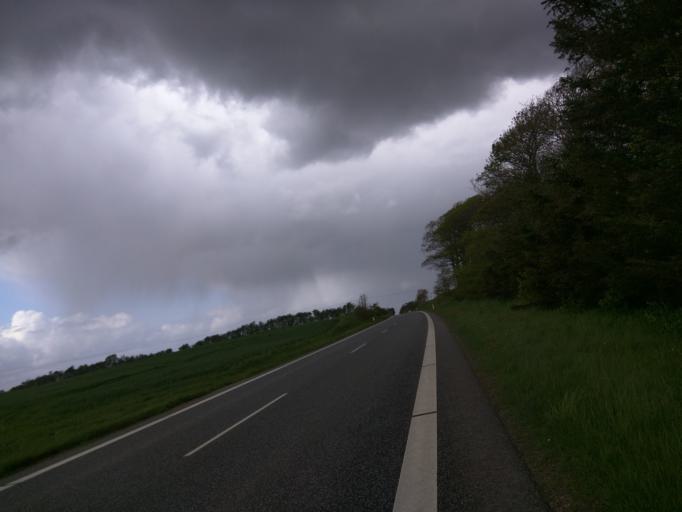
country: DK
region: Central Jutland
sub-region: Silkeborg Kommune
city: Kjellerup
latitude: 56.3466
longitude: 9.4329
